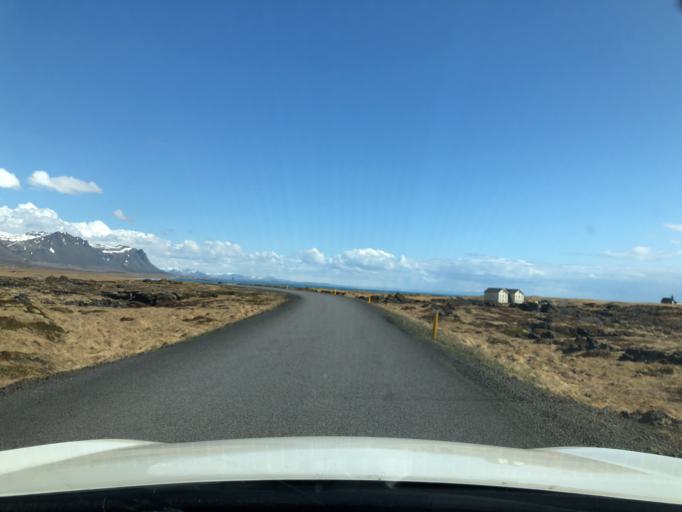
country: IS
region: West
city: Olafsvik
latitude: 64.8250
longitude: -23.3929
